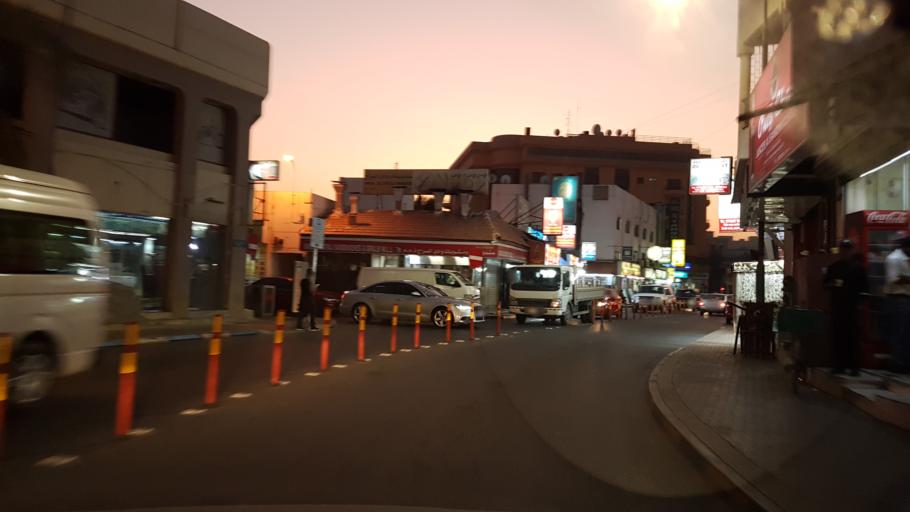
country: BH
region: Manama
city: Manama
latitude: 26.2155
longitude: 50.5909
